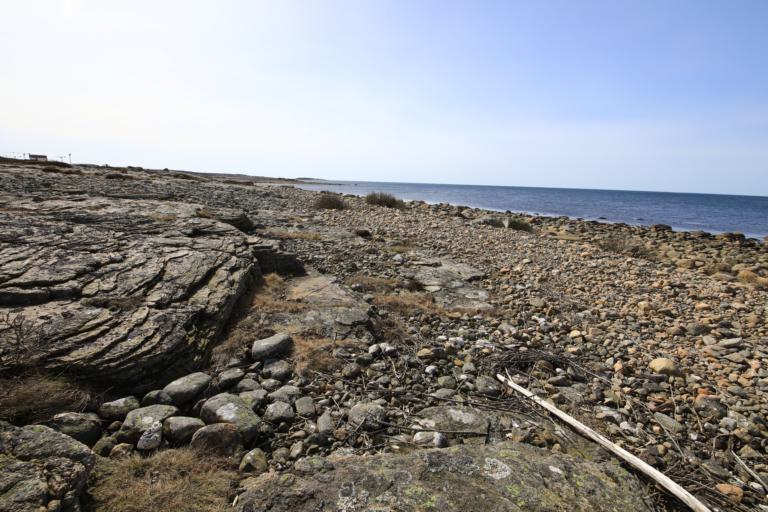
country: SE
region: Halland
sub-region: Kungsbacka Kommun
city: Frillesas
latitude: 57.2710
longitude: 12.1099
